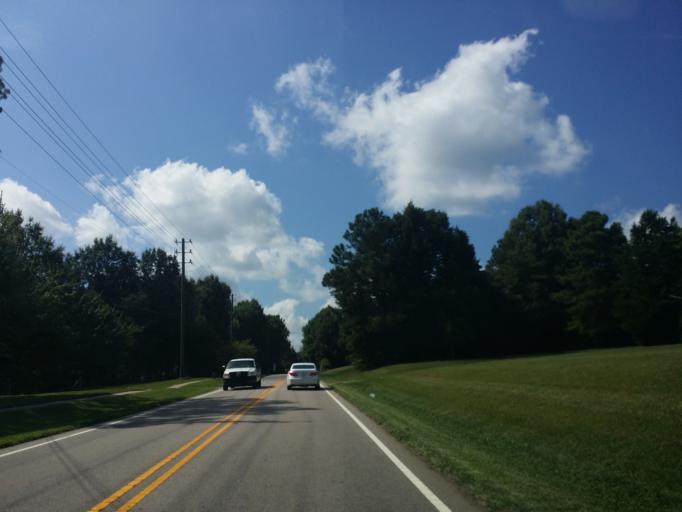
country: US
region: North Carolina
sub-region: Wake County
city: West Raleigh
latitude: 35.8906
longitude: -78.7137
